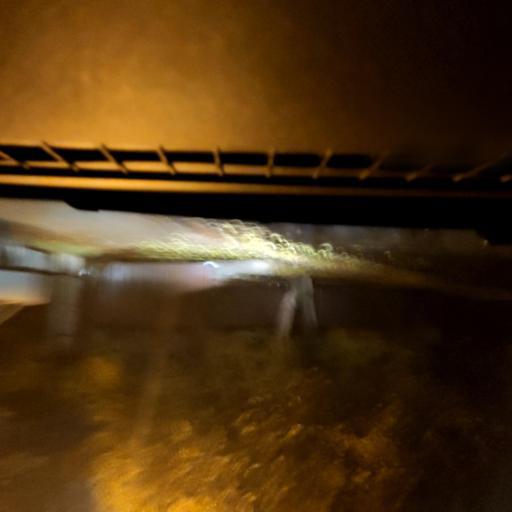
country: RU
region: Voronezj
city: Voronezh
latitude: 51.6514
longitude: 39.1992
